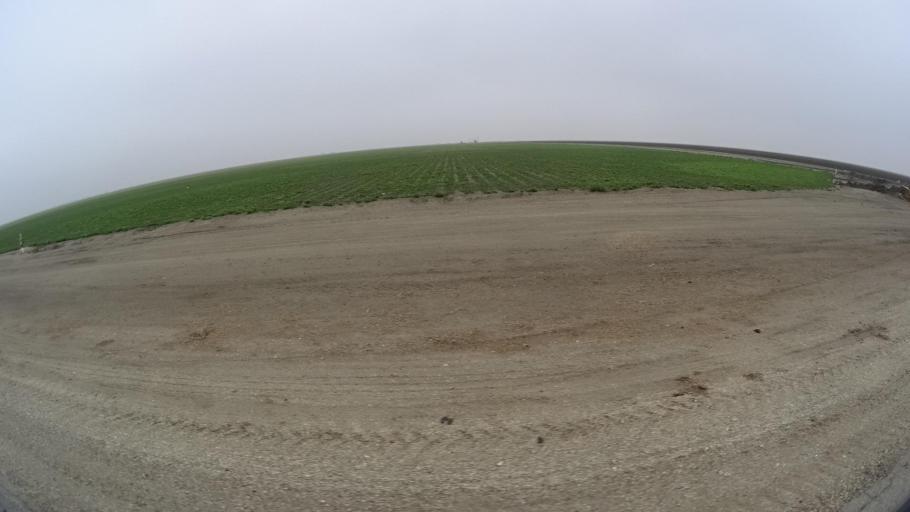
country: US
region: California
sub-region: Kern County
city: Rosedale
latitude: 35.1944
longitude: -119.2163
